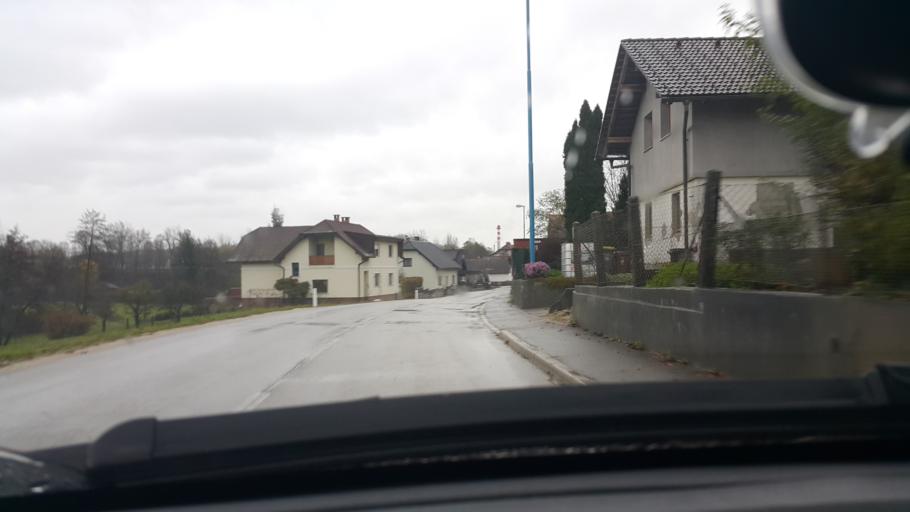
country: SI
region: Medvode
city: Medvode
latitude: 46.1425
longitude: 14.3866
